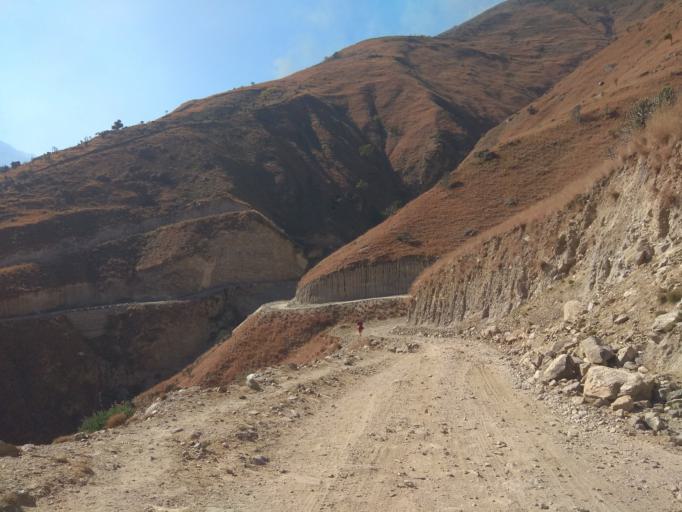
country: NP
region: Mid Western
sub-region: Karnali Zone
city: Jumla
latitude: 29.3002
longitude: 81.7443
